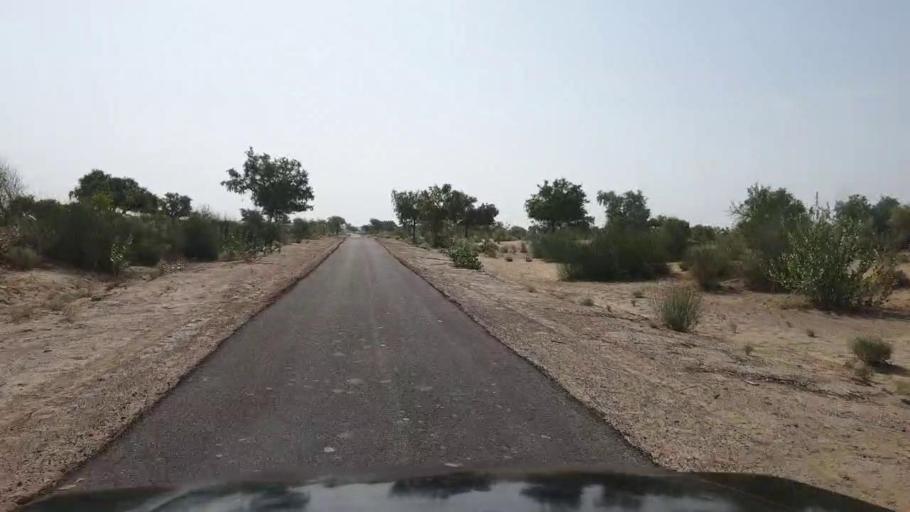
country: PK
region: Sindh
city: Islamkot
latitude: 24.9379
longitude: 70.0883
